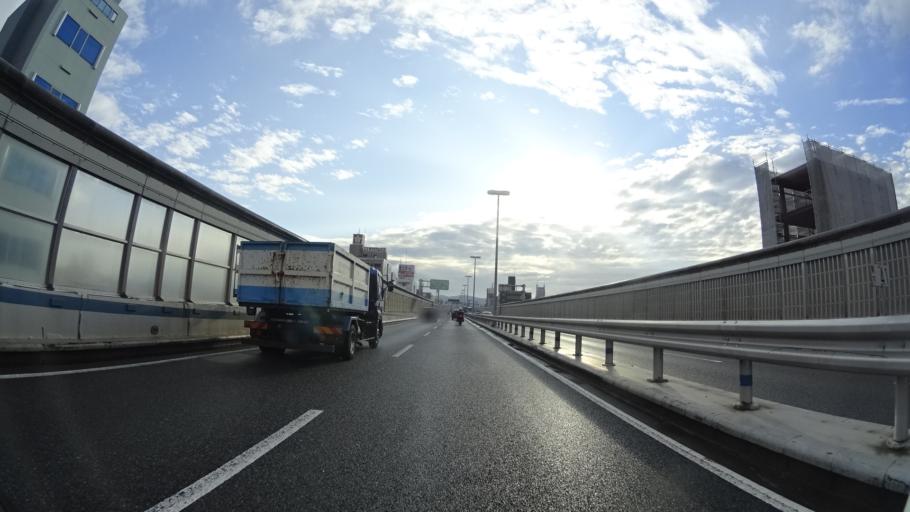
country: JP
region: Osaka
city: Osaka-shi
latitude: 34.6797
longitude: 135.5525
